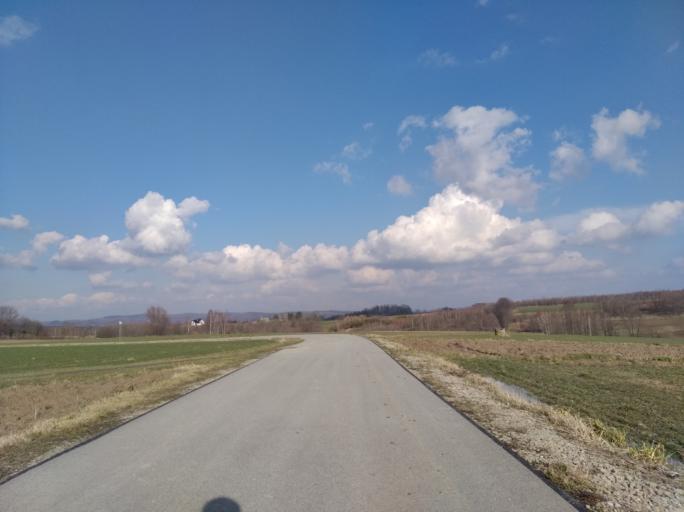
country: PL
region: Subcarpathian Voivodeship
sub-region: Powiat strzyzowski
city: Wysoka Strzyzowska
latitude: 49.8477
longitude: 21.7092
